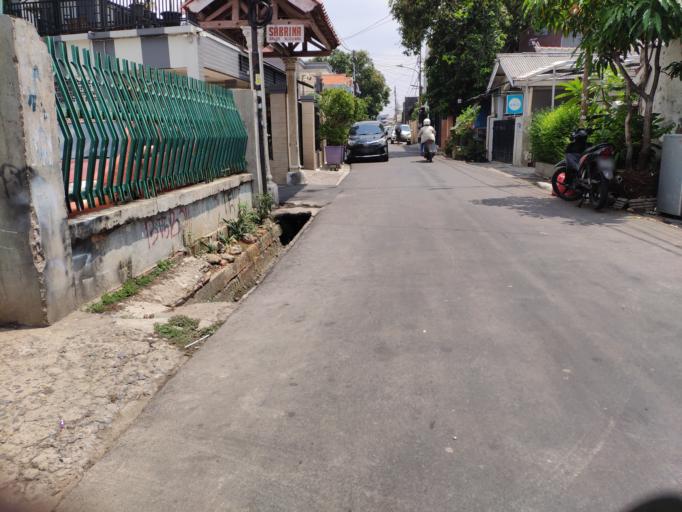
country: ID
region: Jakarta Raya
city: Jakarta
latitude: -6.2103
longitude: 106.8653
